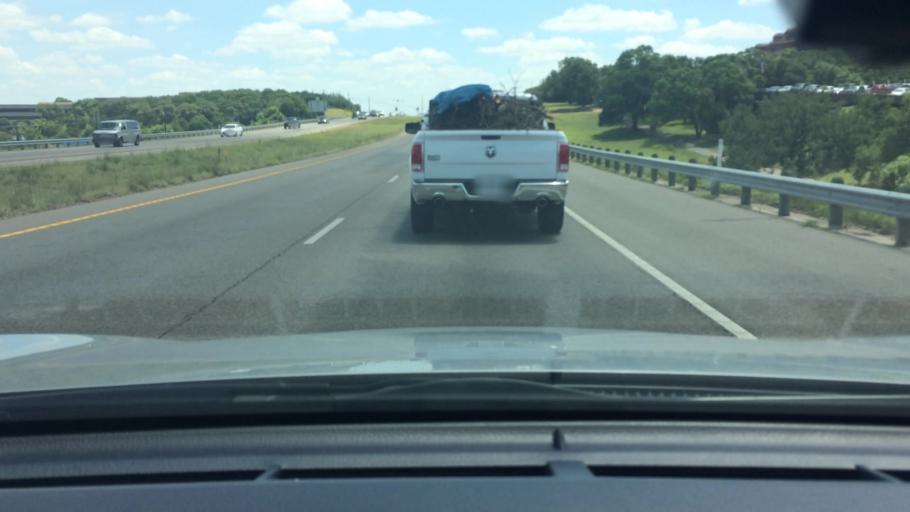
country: US
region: Texas
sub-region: Travis County
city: Lost Creek
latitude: 30.2823
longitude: -97.8234
